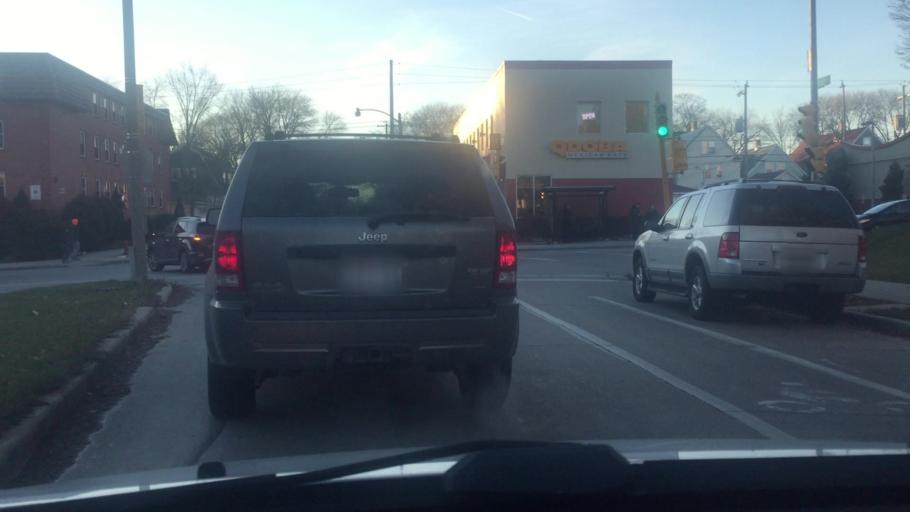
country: US
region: Wisconsin
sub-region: Milwaukee County
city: Shorewood
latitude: 43.0747
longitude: -87.8875
